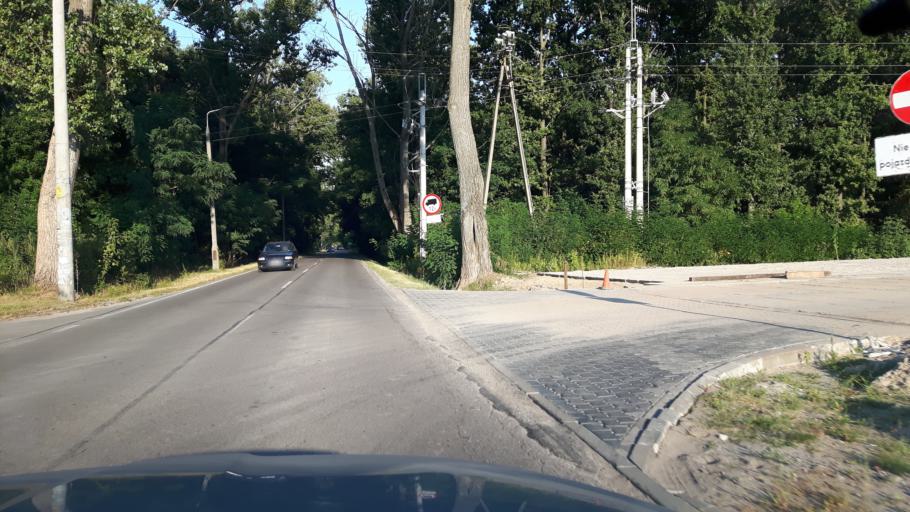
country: PL
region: Masovian Voivodeship
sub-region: Powiat wolominski
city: Slupno
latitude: 52.3650
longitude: 21.1432
